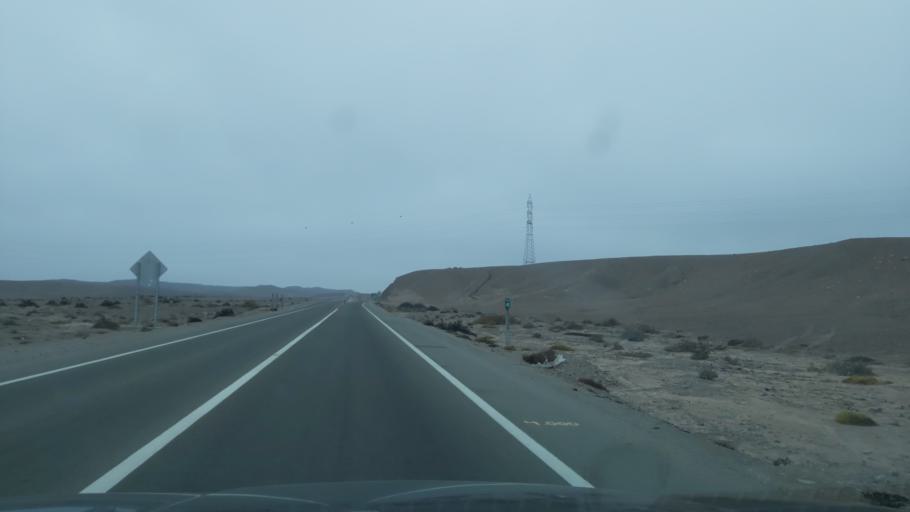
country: CL
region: Atacama
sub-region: Provincia de Copiapo
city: Copiapo
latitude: -27.2900
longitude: -70.1489
